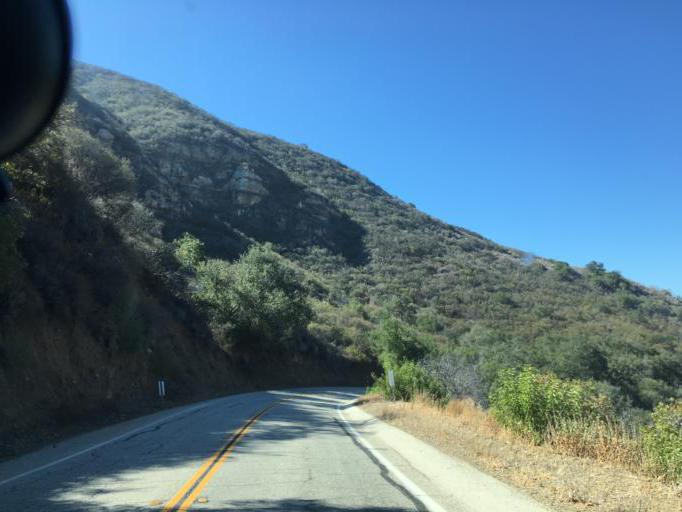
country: US
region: California
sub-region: Ventura County
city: Casa Conejo
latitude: 34.0700
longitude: -118.9289
